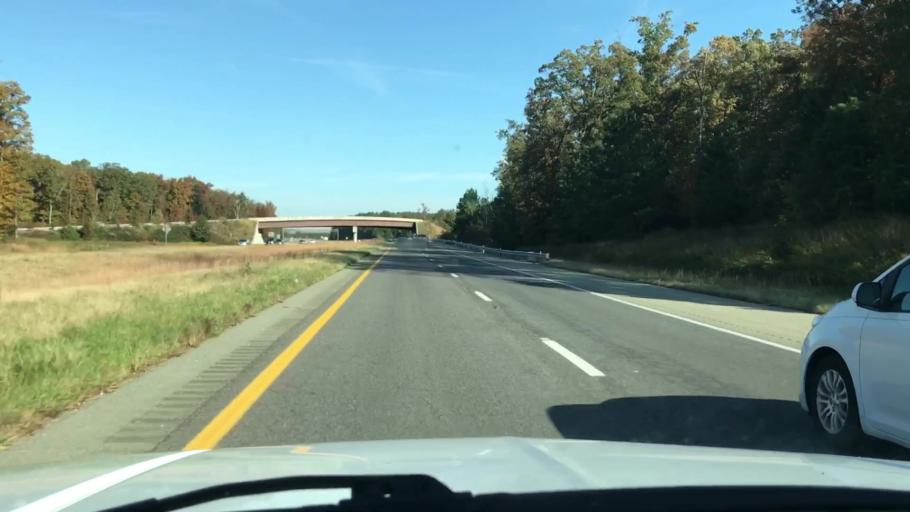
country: US
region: Virginia
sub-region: Henrico County
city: Short Pump
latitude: 37.6345
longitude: -77.6637
